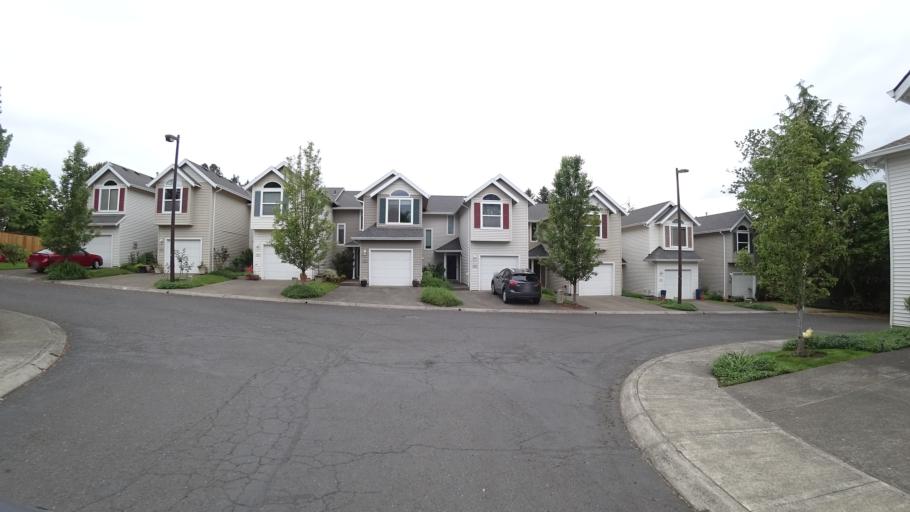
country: US
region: Oregon
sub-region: Washington County
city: Beaverton
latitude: 45.4754
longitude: -122.8103
